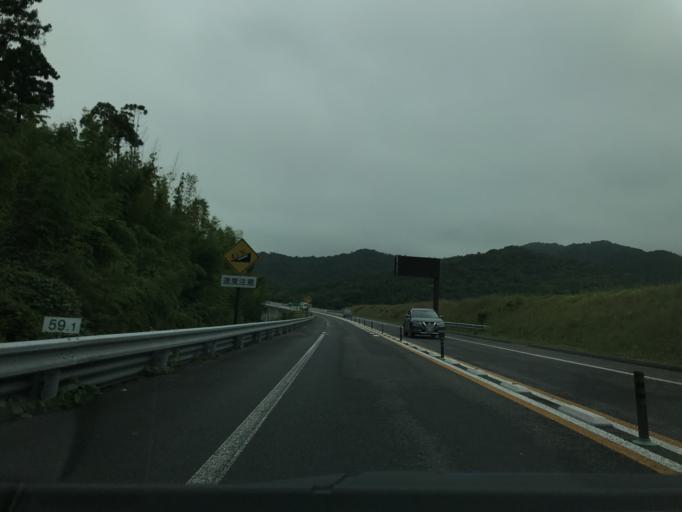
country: JP
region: Fukuoka
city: Nakatsu
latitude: 33.5059
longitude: 131.2958
